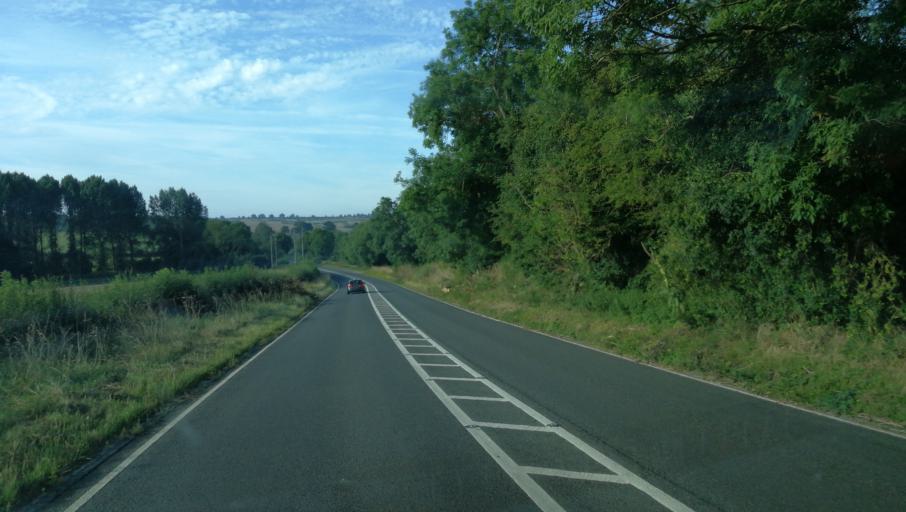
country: GB
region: England
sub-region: Oxfordshire
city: Deddington
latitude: 51.9708
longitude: -1.3191
